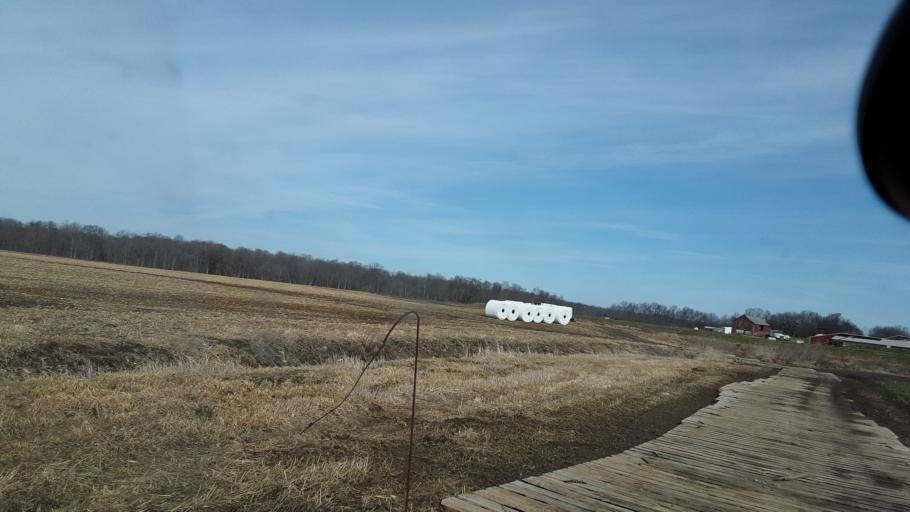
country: US
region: Ohio
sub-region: Licking County
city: Hebron
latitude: 39.9700
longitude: -82.4605
